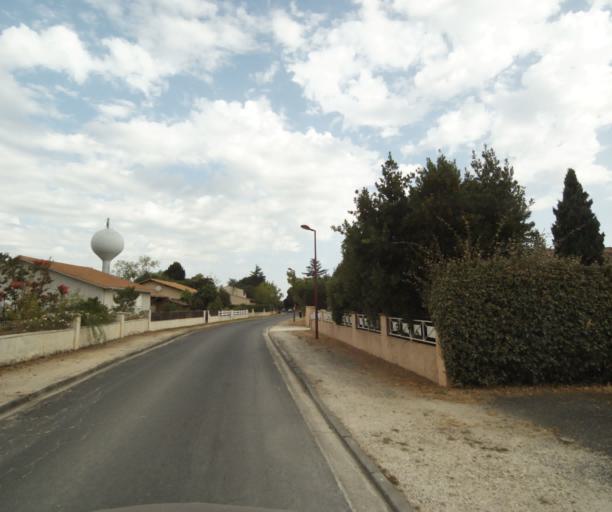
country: FR
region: Aquitaine
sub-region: Departement de la Gironde
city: Creon
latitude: 44.7694
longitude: -0.3441
